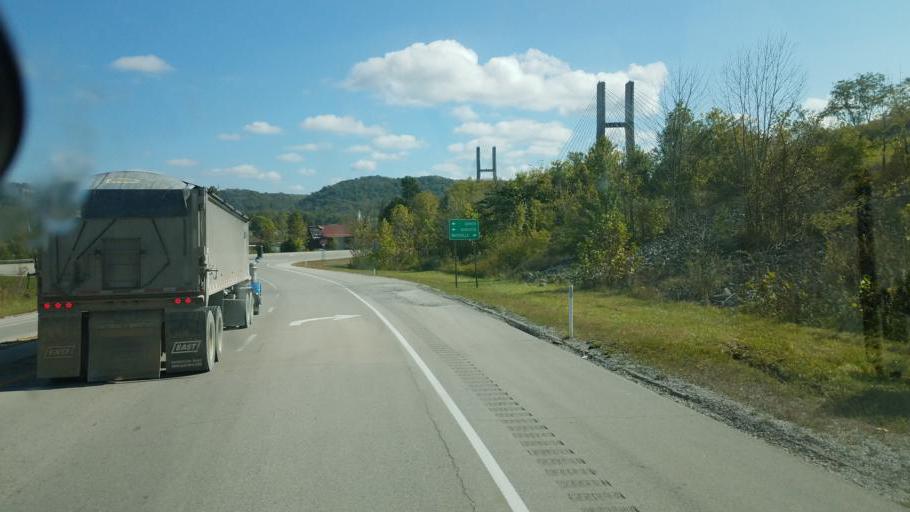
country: US
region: Ohio
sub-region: Brown County
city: Aberdeen
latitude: 38.6846
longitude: -83.7885
